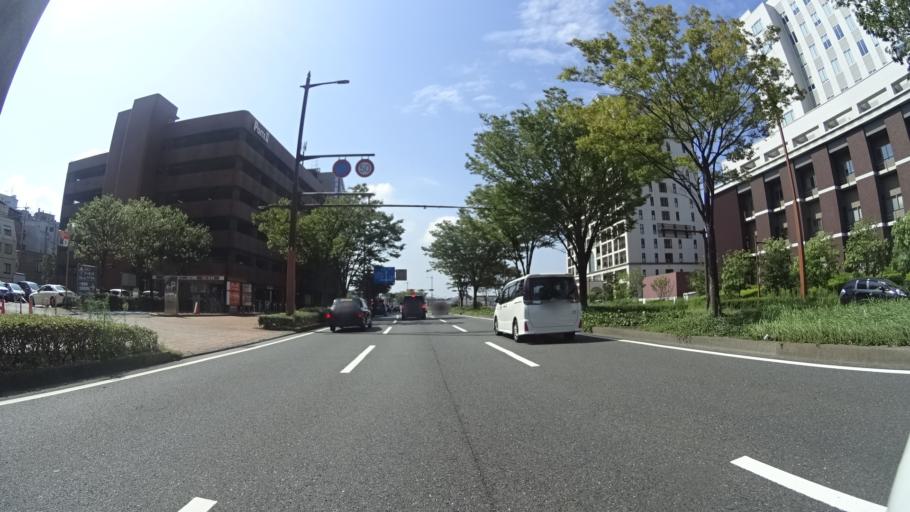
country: JP
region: Fukuoka
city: Kitakyushu
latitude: 33.8895
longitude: 130.8827
